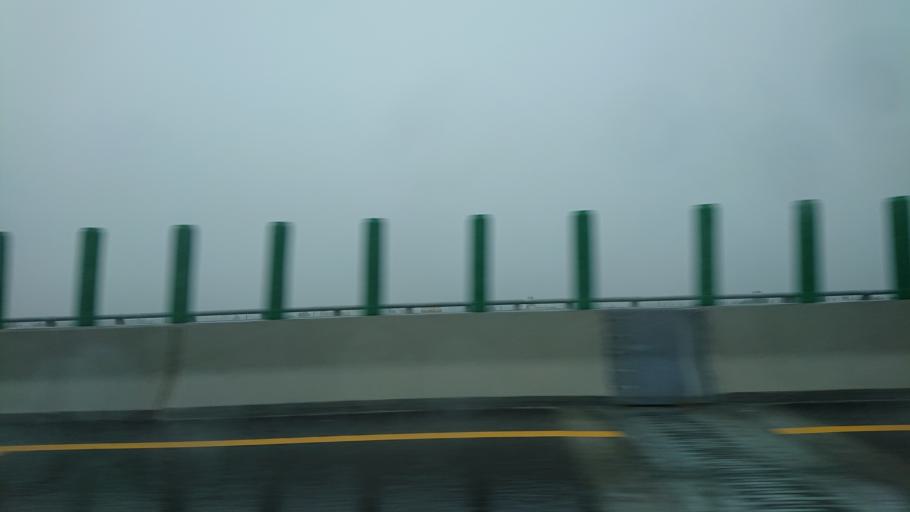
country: TW
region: Taiwan
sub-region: Changhua
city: Chang-hua
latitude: 23.9091
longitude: 120.3063
